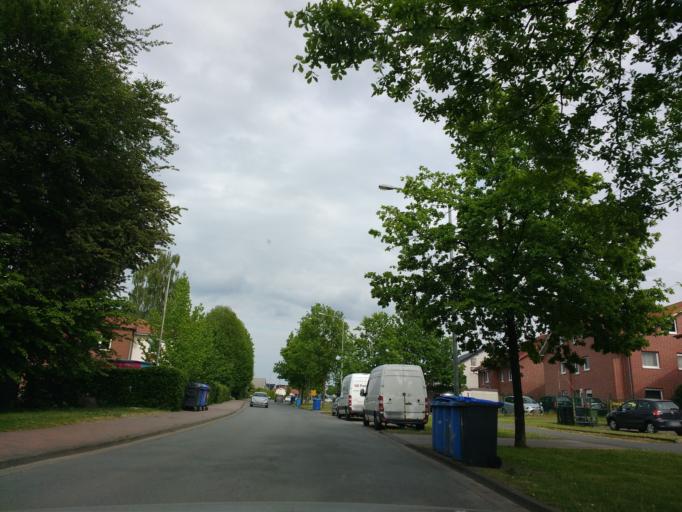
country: DE
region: North Rhine-Westphalia
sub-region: Regierungsbezirk Detmold
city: Salzkotten
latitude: 51.6705
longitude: 8.6163
